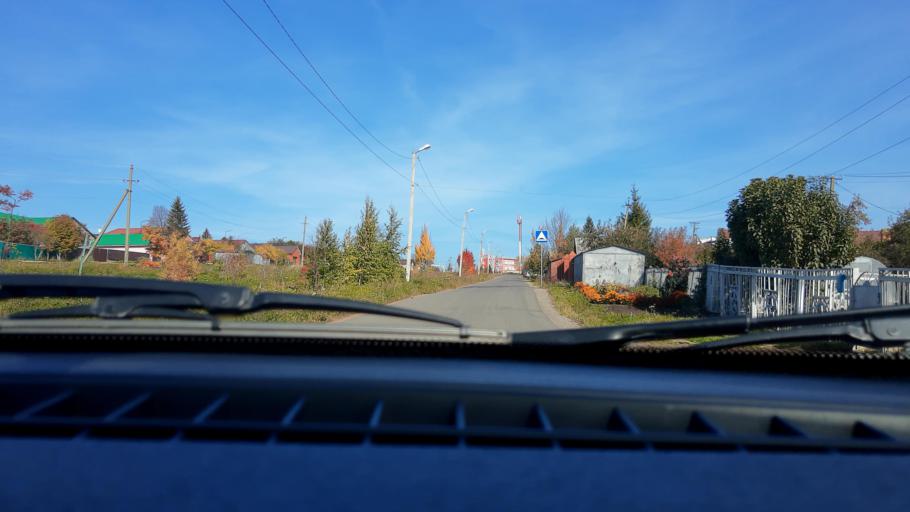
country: RU
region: Bashkortostan
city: Mikhaylovka
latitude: 54.8103
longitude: 55.8923
